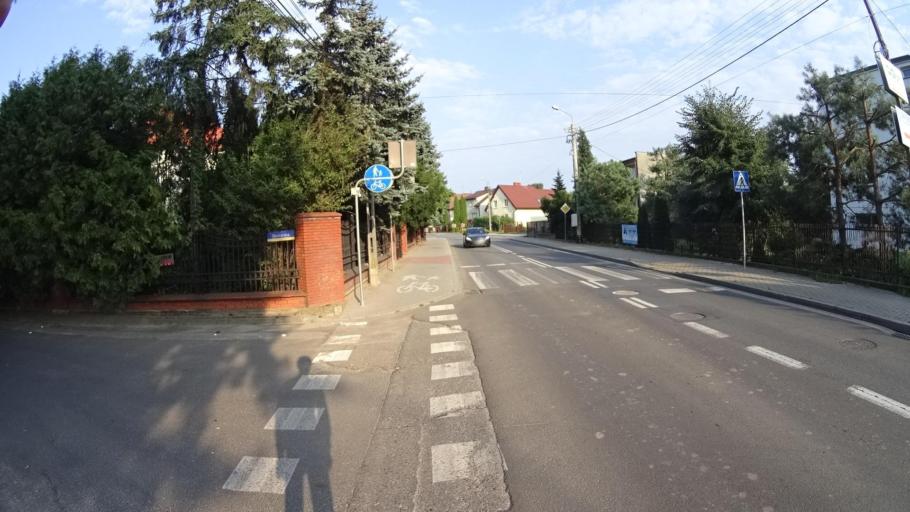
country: PL
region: Masovian Voivodeship
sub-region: Powiat pruszkowski
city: Rybie
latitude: 52.1456
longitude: 20.9497
